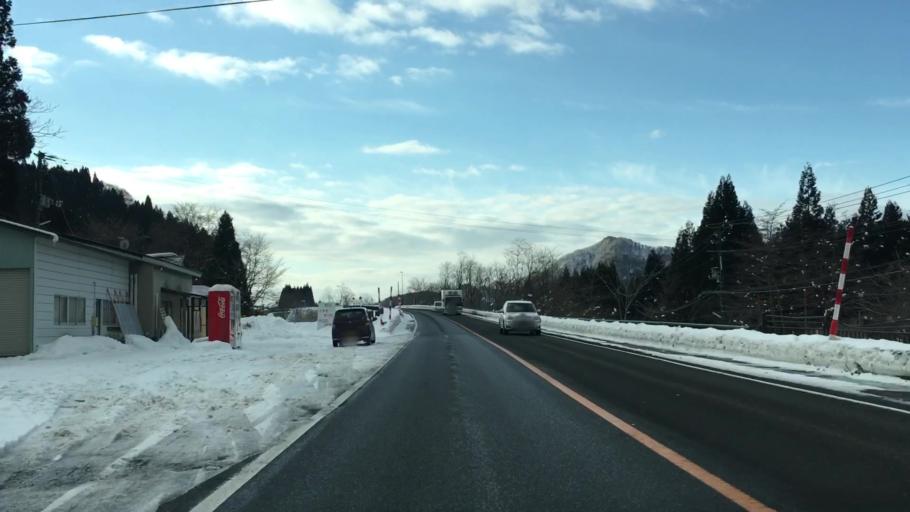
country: JP
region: Akita
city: Odate
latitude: 40.3983
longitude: 140.6063
